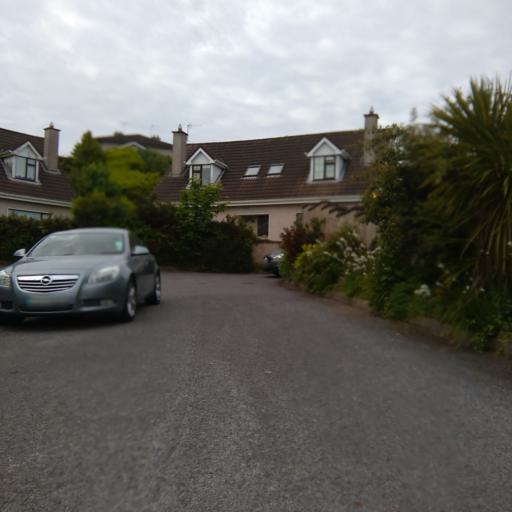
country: IE
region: Munster
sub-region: County Cork
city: Cork
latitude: 51.9131
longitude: -8.4464
